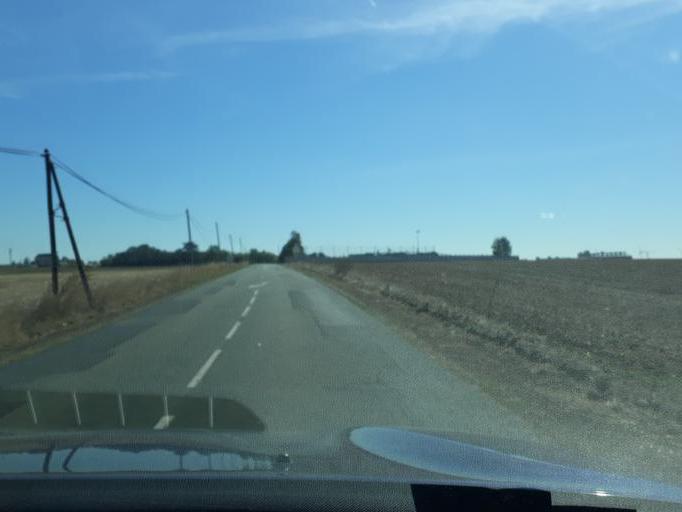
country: FR
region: Centre
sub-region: Departement du Loir-et-Cher
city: Ouzouer-le-Marche
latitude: 47.9244
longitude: 1.5202
